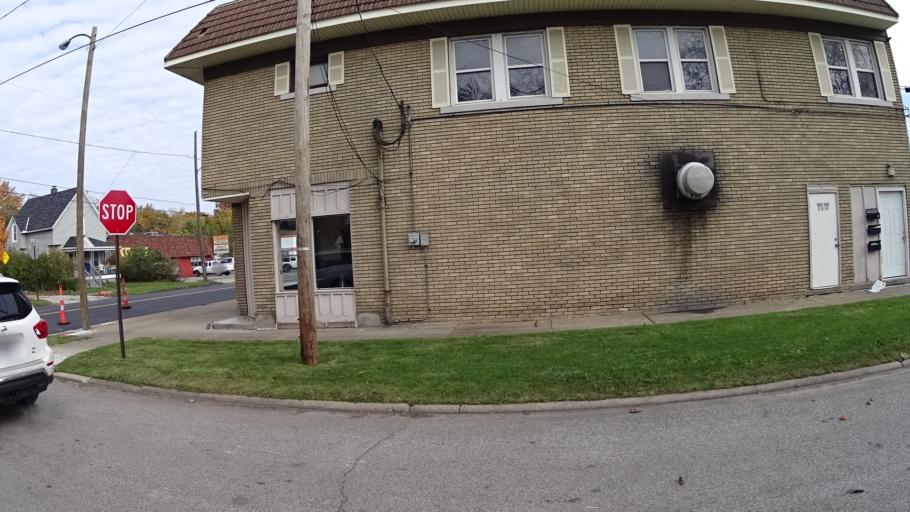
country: US
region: Ohio
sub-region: Lorain County
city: Lorain
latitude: 41.4728
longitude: -82.1667
